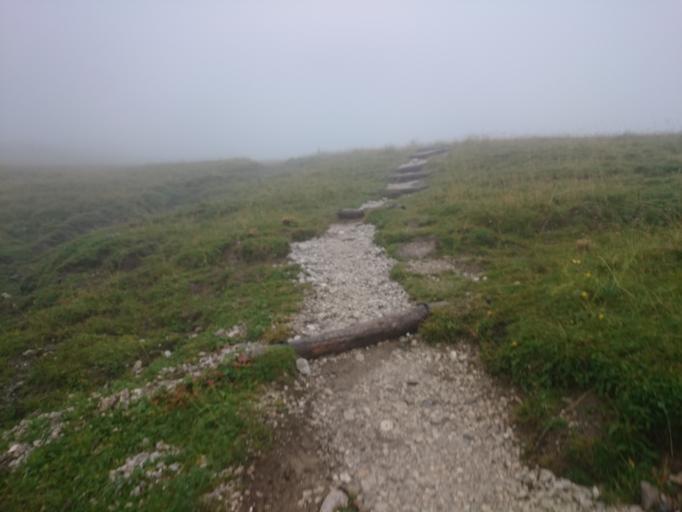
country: AT
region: Tyrol
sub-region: Politischer Bezirk Innsbruck Land
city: Absam
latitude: 47.4017
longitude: 11.4962
